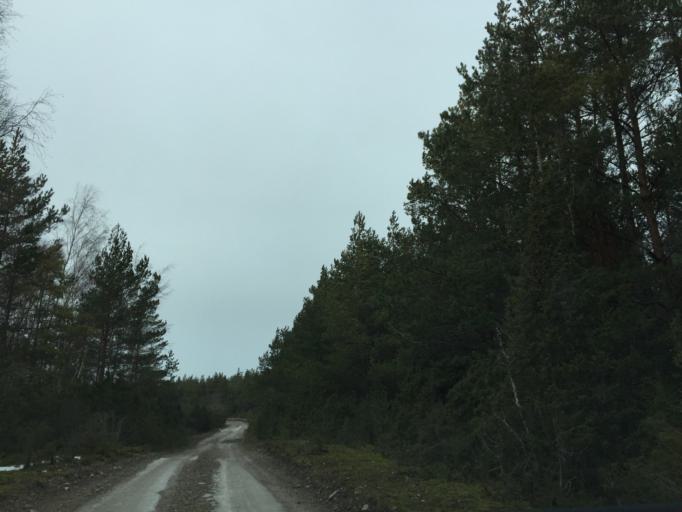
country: EE
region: Saare
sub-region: Kuressaare linn
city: Kuressaare
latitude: 58.5005
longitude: 21.9199
